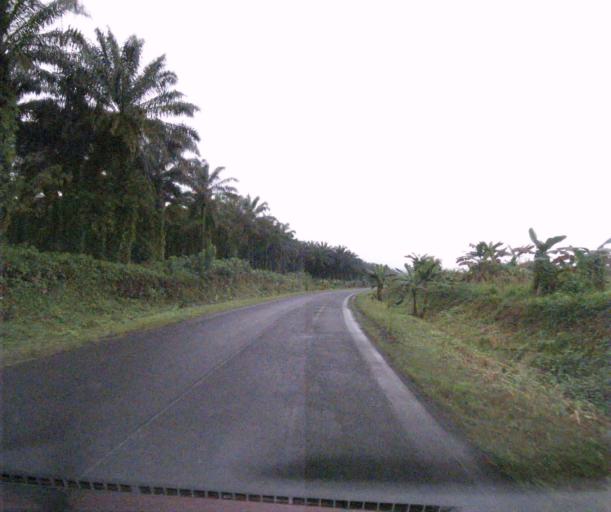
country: CM
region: South-West Province
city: Idenao
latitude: 4.2005
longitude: 9.0014
